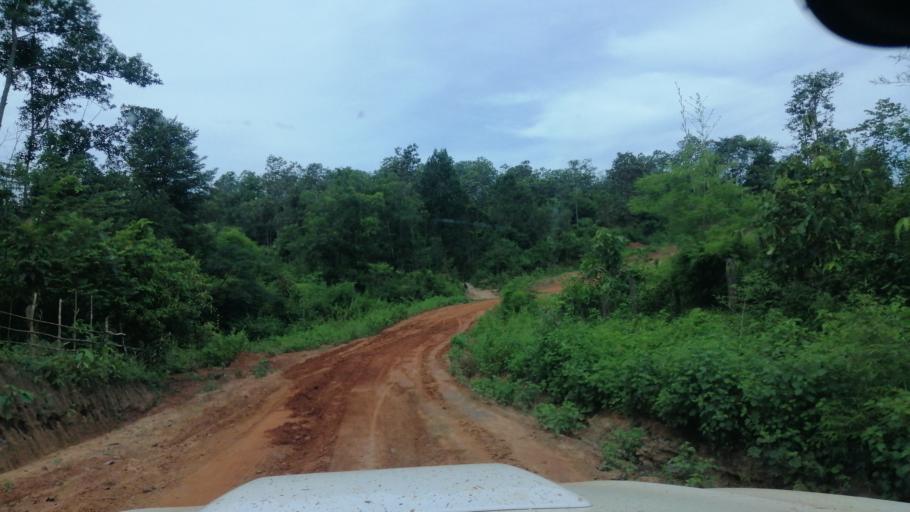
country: TH
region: Loei
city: Na Haeo
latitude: 17.5780
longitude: 101.1540
